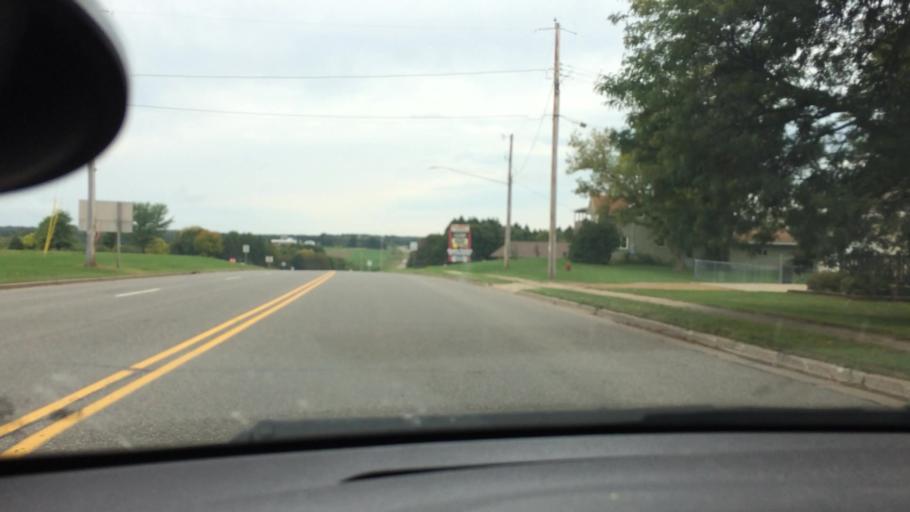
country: US
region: Wisconsin
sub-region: Clark County
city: Neillsville
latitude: 44.5527
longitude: -90.6001
